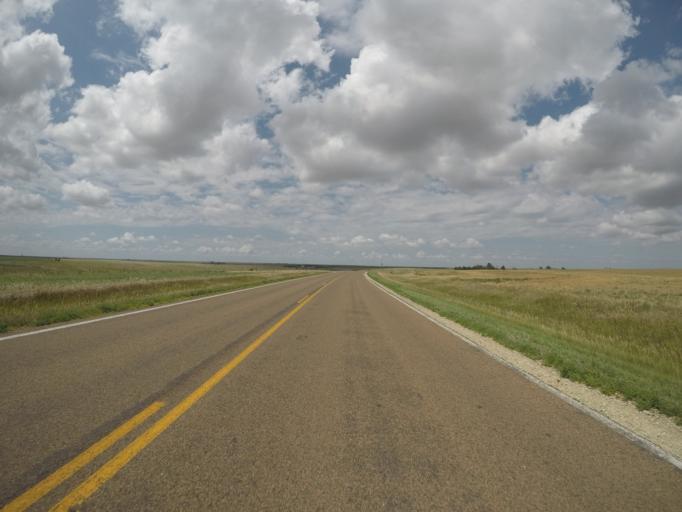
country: US
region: Kansas
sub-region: Rawlins County
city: Atwood
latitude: 39.9134
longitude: -101.0554
